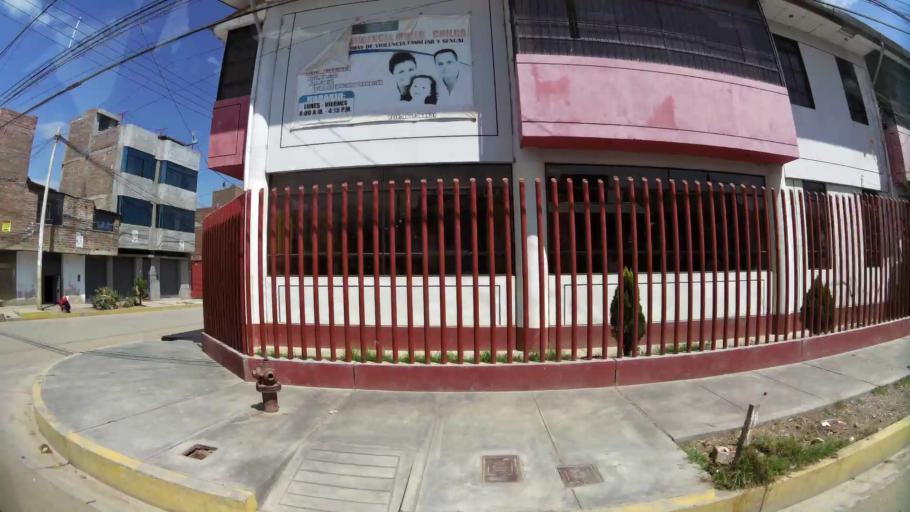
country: PE
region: Junin
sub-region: Provincia de Huancayo
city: El Tambo
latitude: -12.0832
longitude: -75.2101
